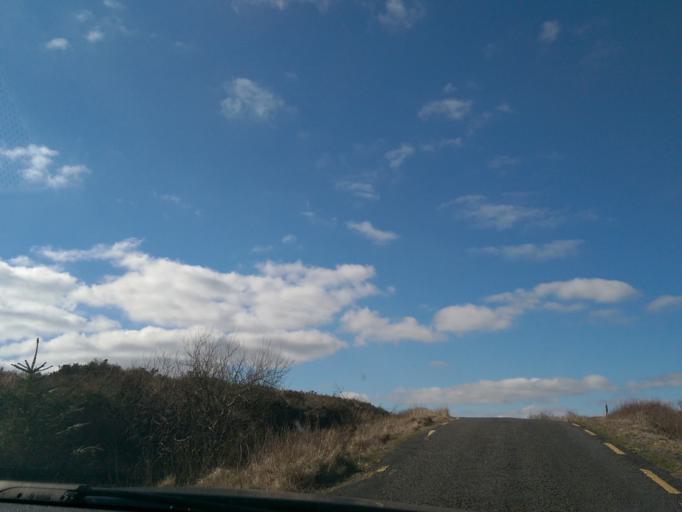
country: IE
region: Leinster
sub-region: Laois
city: Mountrath
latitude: 53.0807
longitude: -7.5955
